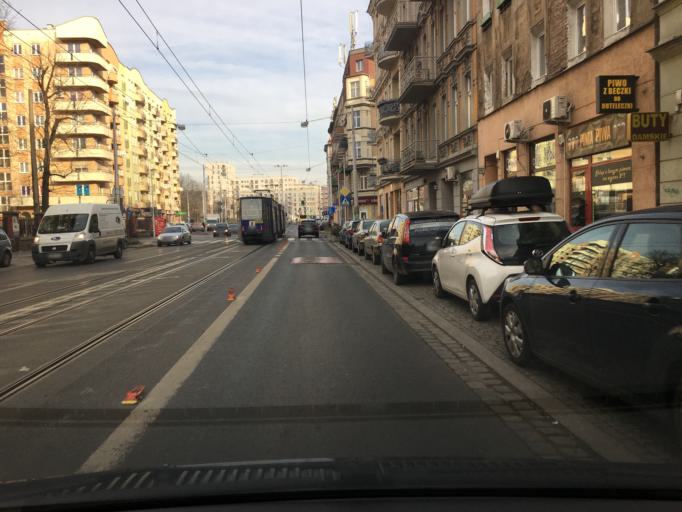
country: PL
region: Lower Silesian Voivodeship
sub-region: Powiat wroclawski
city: Wroclaw
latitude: 51.1224
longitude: 17.0441
